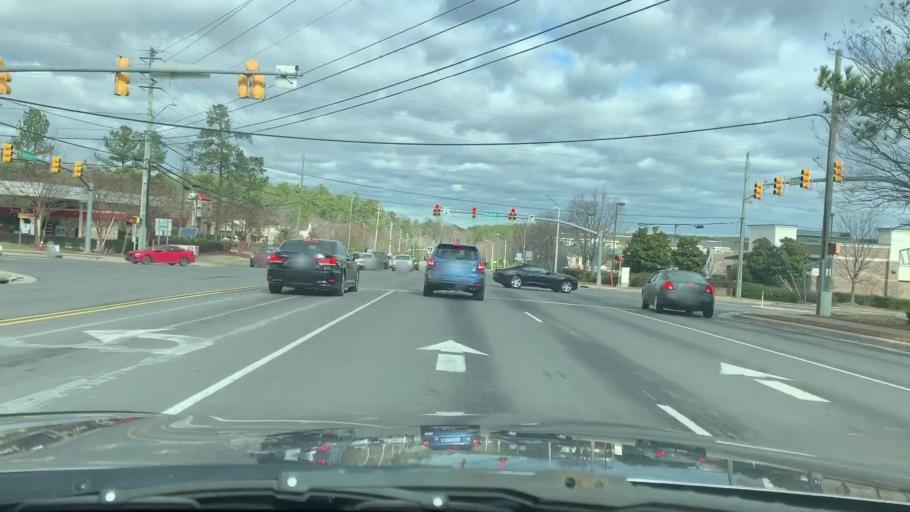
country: US
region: North Carolina
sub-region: Wake County
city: Cary
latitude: 35.8023
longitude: -78.7829
